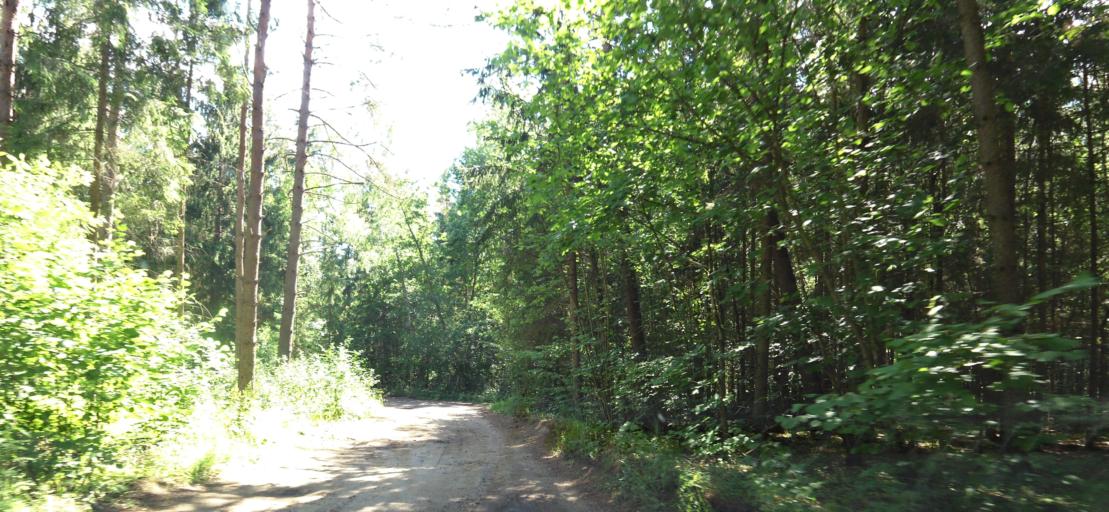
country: LT
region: Vilnius County
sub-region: Vilnius
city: Fabijoniskes
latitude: 54.8276
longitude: 25.3210
